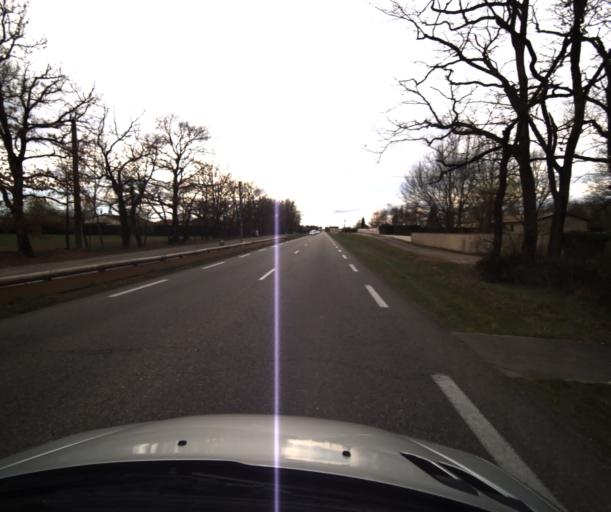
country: FR
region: Midi-Pyrenees
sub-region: Departement du Tarn-et-Garonne
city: Saint-Etienne-de-Tulmont
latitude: 44.0439
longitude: 1.4417
